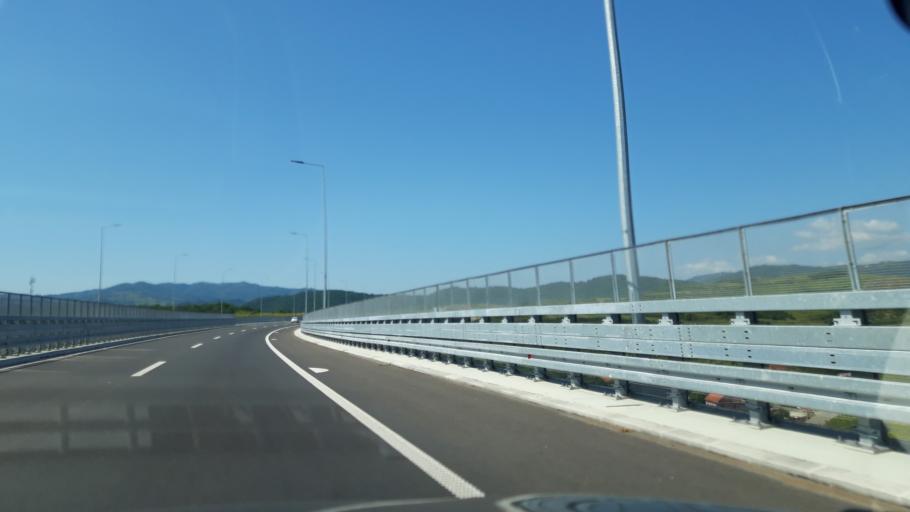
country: RS
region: Central Serbia
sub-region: Pcinjski Okrug
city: Vladicin Han
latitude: 42.7084
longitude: 22.0725
